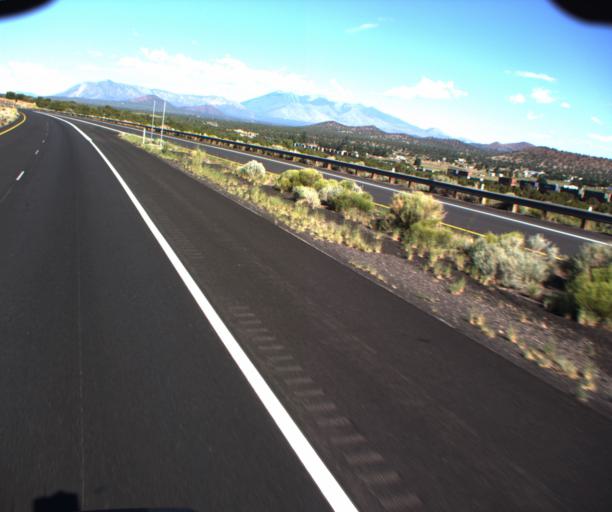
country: US
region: Arizona
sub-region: Coconino County
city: Flagstaff
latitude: 35.2027
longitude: -111.4102
